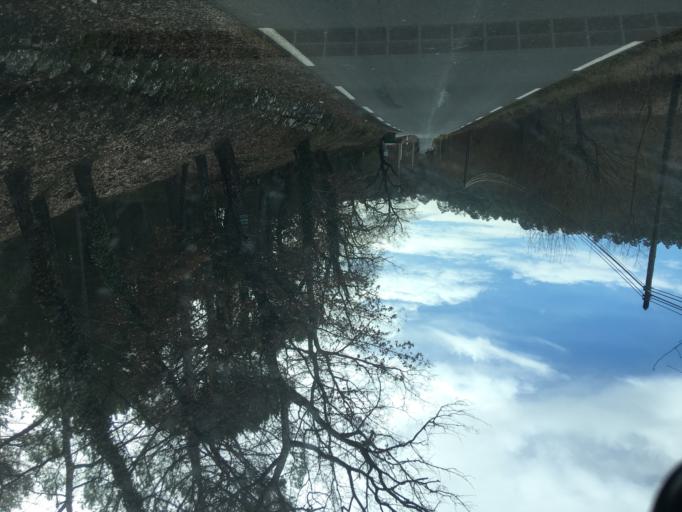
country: FR
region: Provence-Alpes-Cote d'Azur
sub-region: Departement du Var
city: Bras
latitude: 43.4599
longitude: 5.9650
